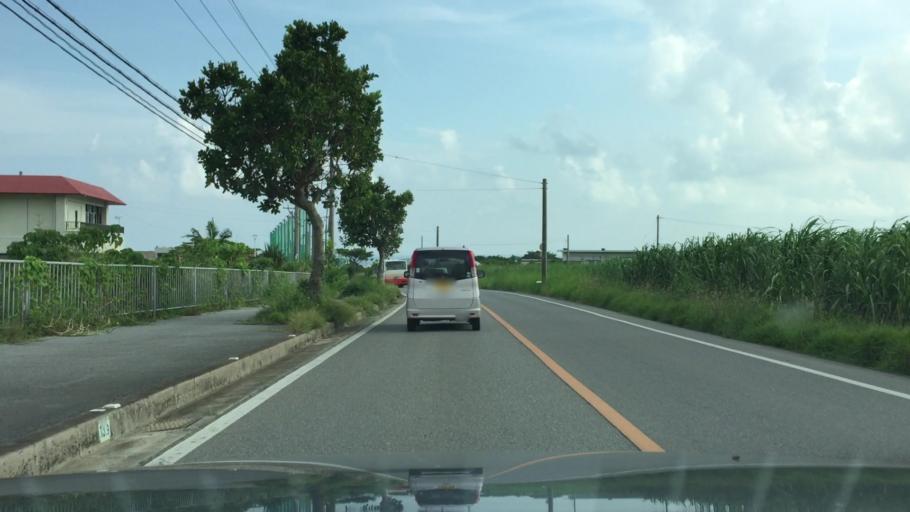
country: JP
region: Okinawa
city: Ishigaki
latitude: 24.3592
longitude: 124.1742
